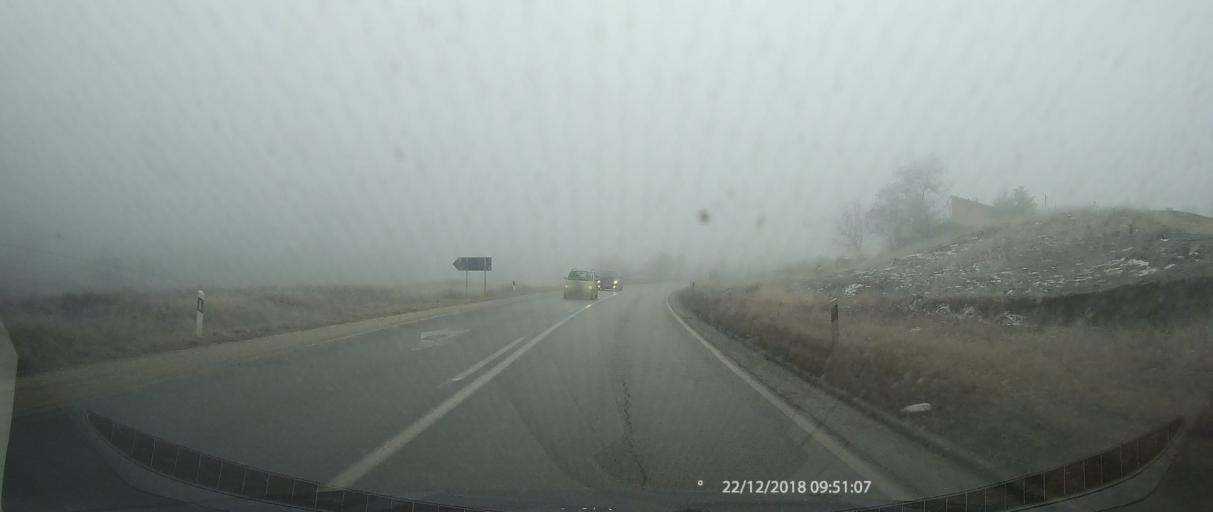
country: MK
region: Staro Nagoricane
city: Staro Nagorichane
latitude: 42.1732
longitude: 21.8005
